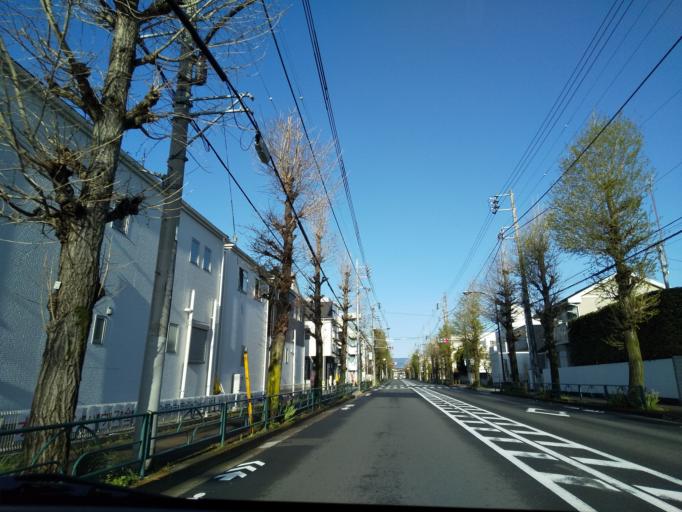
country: JP
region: Tokyo
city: Hino
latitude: 35.6593
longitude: 139.3653
